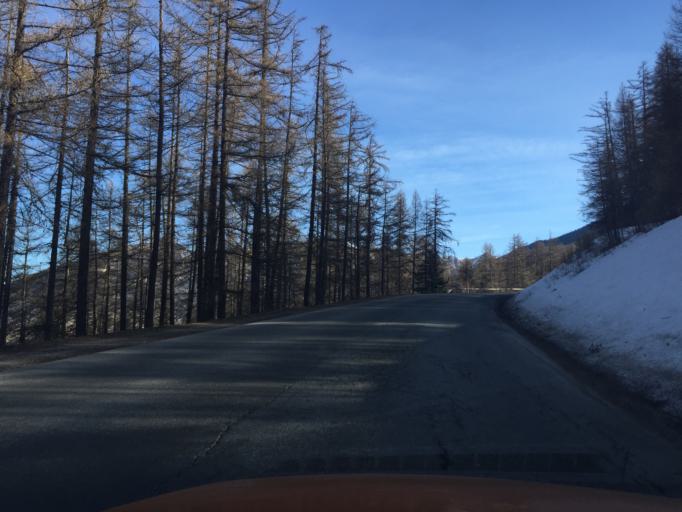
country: FR
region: Provence-Alpes-Cote d'Azur
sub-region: Departement des Hautes-Alpes
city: Embrun
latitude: 44.4860
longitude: 6.5512
